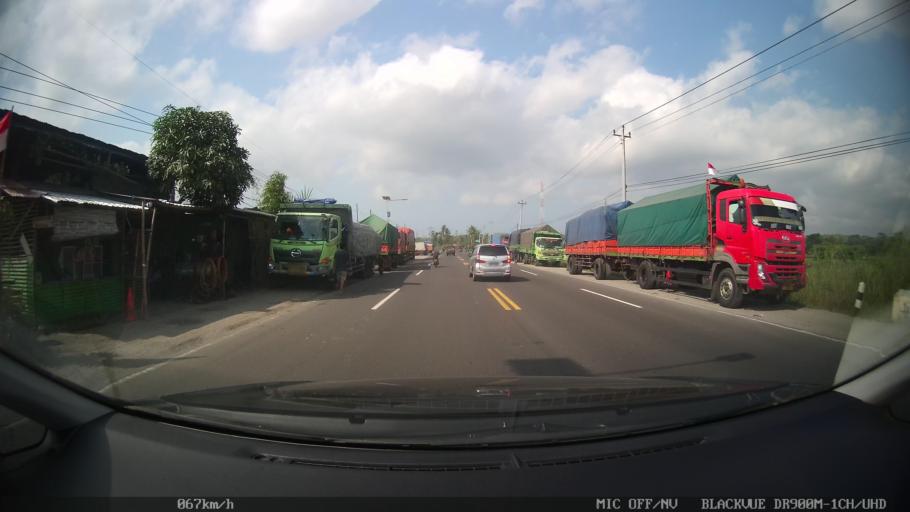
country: ID
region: Daerah Istimewa Yogyakarta
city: Srandakan
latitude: -7.8721
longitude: 110.2082
